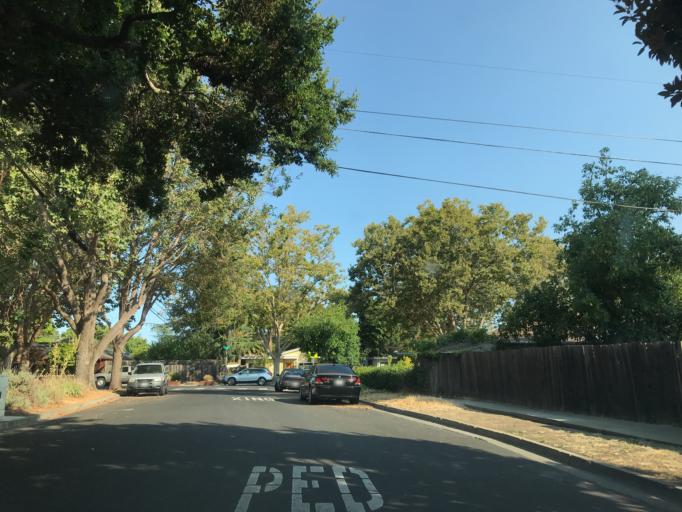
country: US
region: California
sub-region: San Mateo County
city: Redwood City
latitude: 37.4949
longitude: -122.2396
